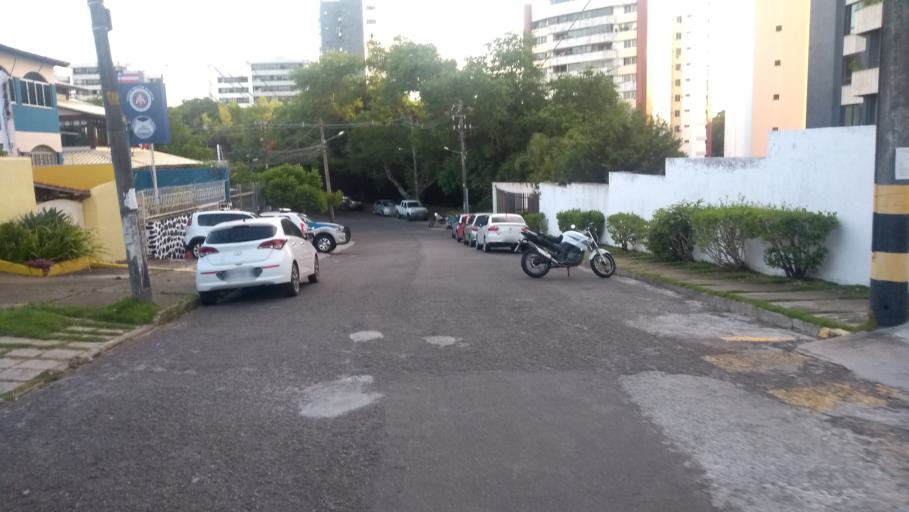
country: BR
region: Bahia
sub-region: Salvador
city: Salvador
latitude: -12.9908
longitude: -38.4660
